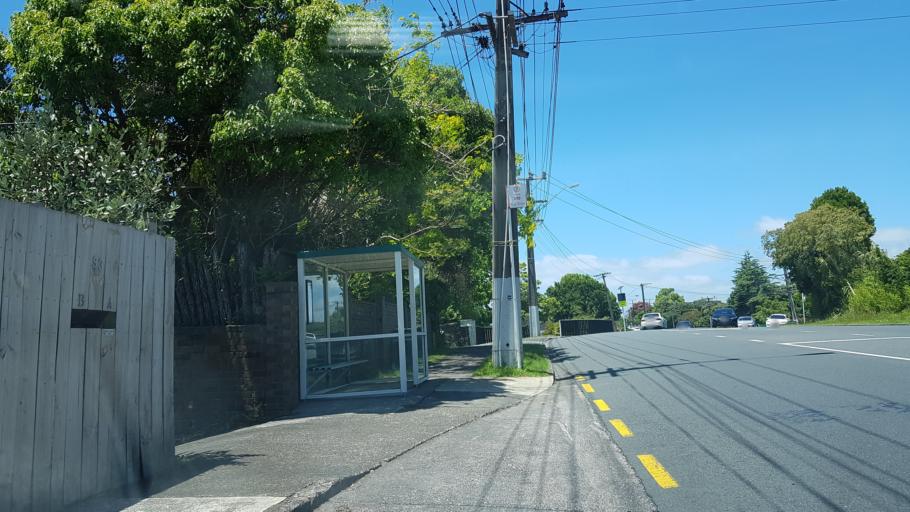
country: NZ
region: Auckland
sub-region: Auckland
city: North Shore
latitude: -36.7873
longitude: 174.7427
